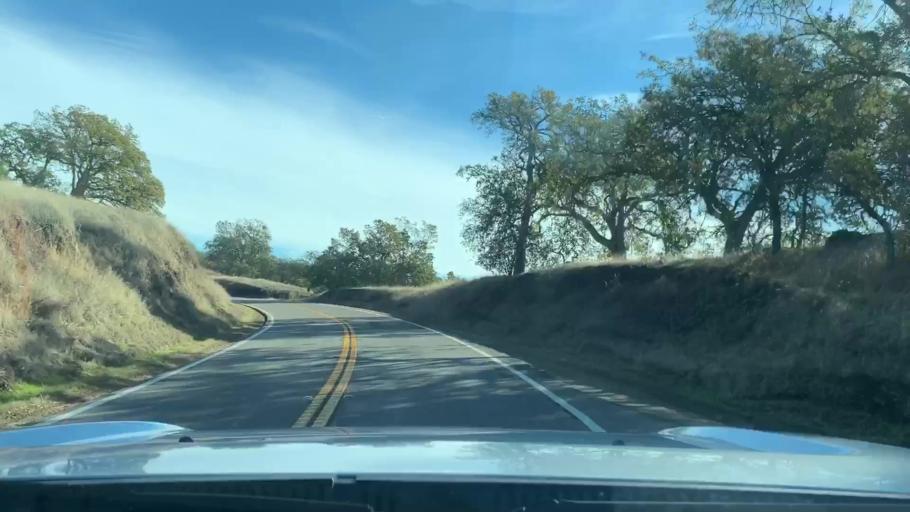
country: US
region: California
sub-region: Monterey County
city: King City
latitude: 36.1923
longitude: -120.7746
